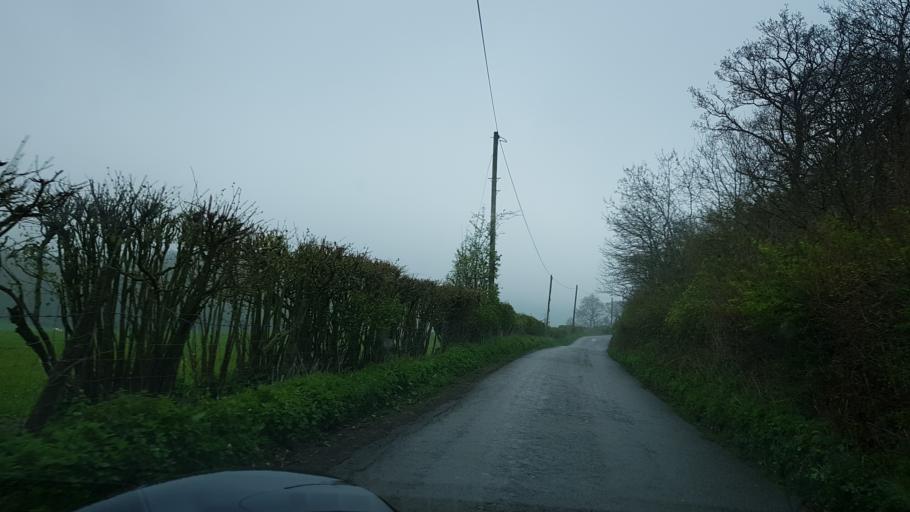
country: GB
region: England
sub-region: Herefordshire
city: Brockhampton
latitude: 52.0256
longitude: -2.5466
